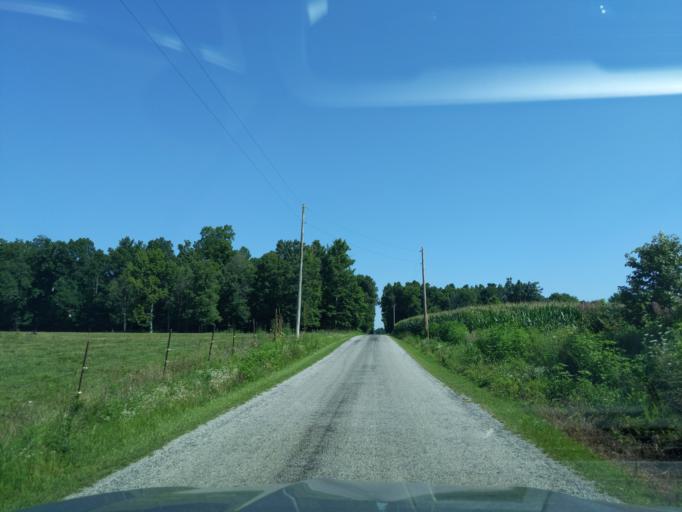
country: US
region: Indiana
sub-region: Ripley County
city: Osgood
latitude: 39.0944
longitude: -85.4325
